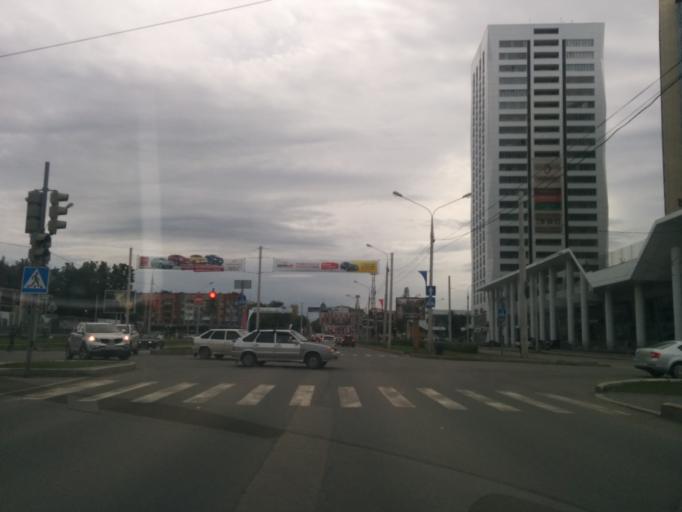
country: RU
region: Perm
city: Perm
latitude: 58.0058
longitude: 56.2579
